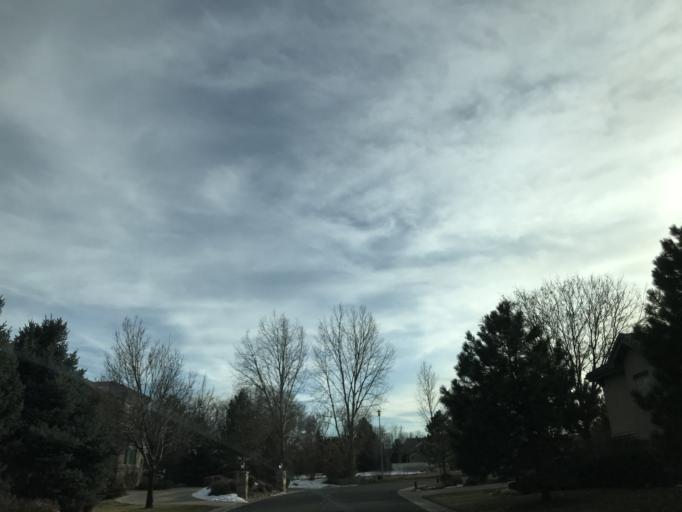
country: US
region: Colorado
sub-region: Arapahoe County
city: Columbine Valley
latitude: 39.6076
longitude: -105.0314
